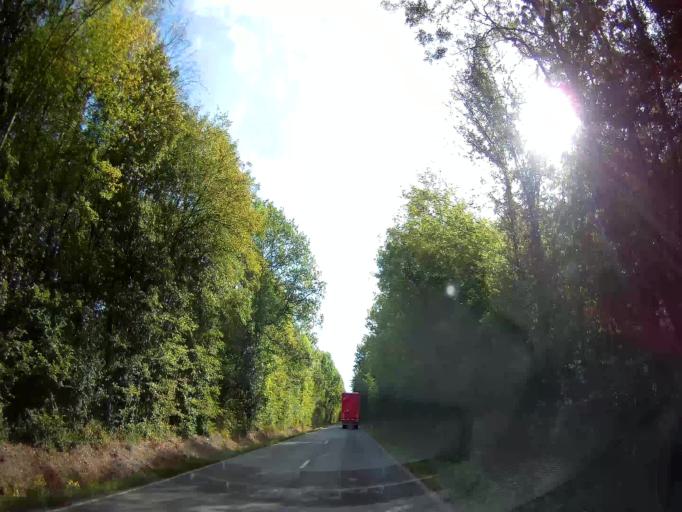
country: BE
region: Wallonia
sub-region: Province de Namur
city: Rochefort
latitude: 50.1671
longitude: 5.1431
